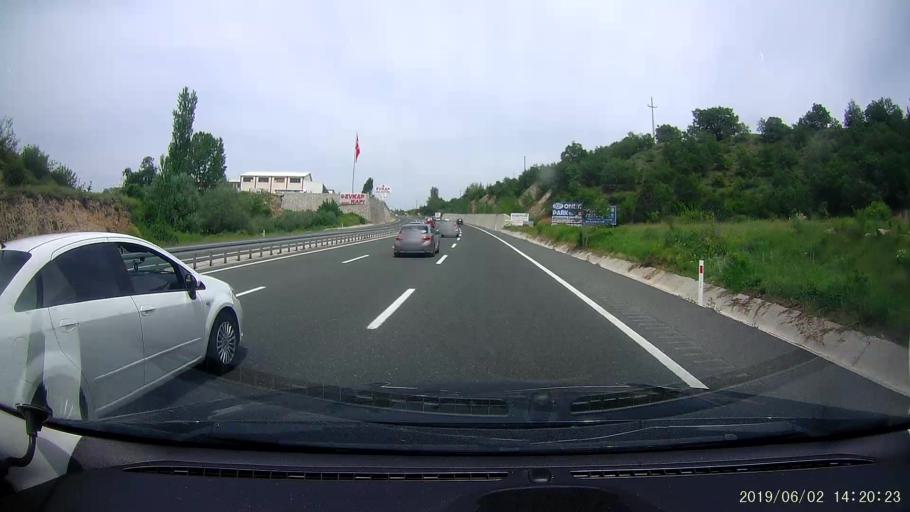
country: TR
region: Kastamonu
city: Tosya
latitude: 40.9693
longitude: 33.9901
